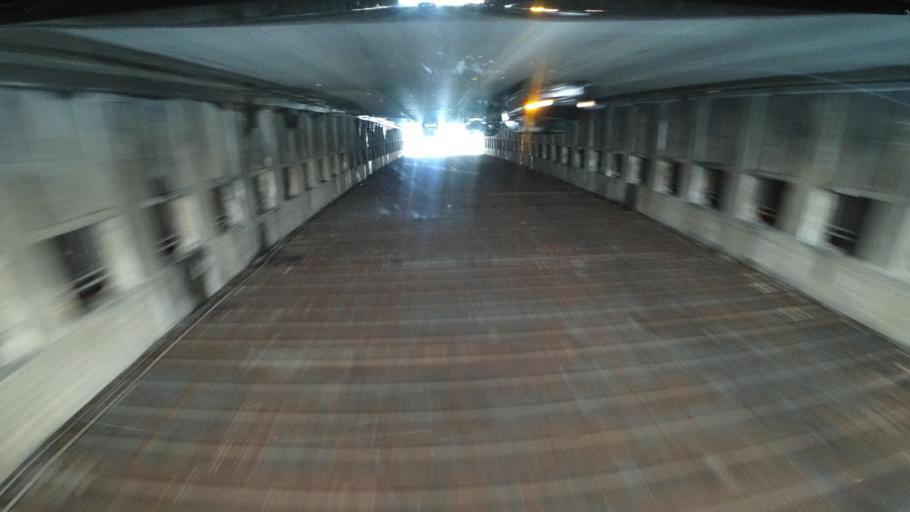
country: US
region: Illinois
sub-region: Cook County
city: Schiller Park
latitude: 41.9657
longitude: -87.8707
